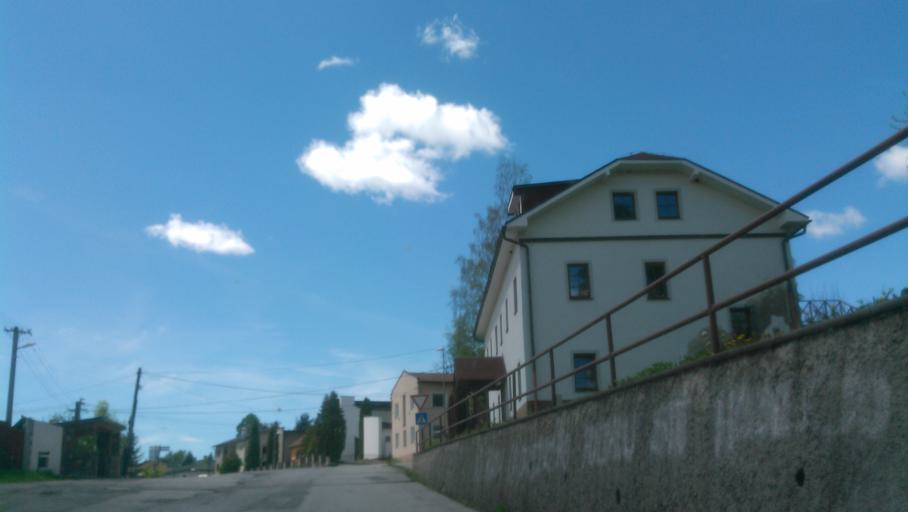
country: SK
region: Banskobystricky
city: Hrochot,Slovakia
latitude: 48.7948
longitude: 19.3822
